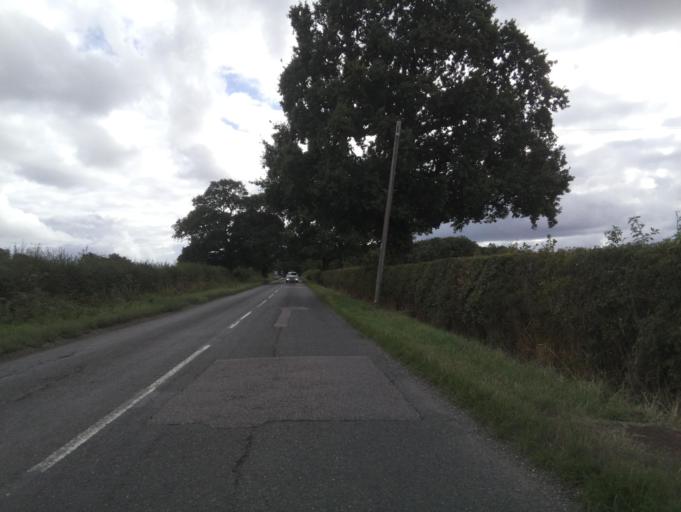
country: GB
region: England
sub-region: Nottinghamshire
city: East Leake
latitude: 52.8174
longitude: -1.1782
